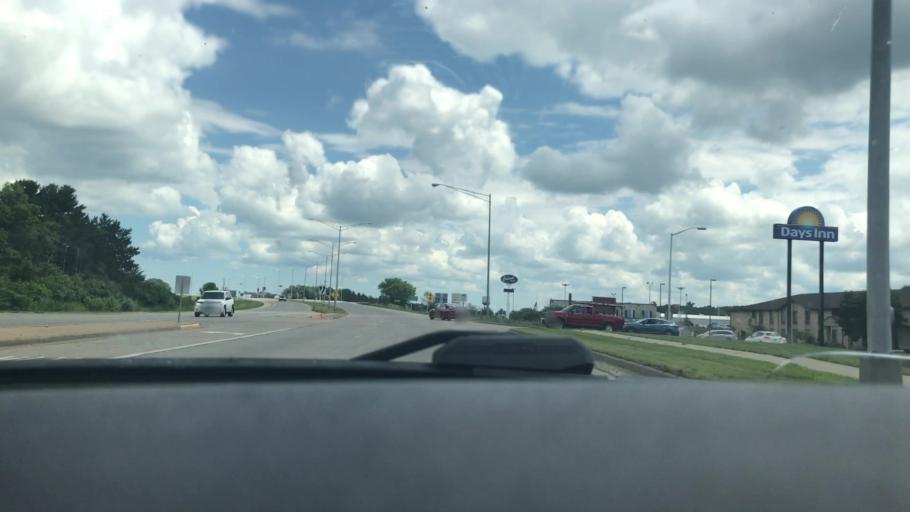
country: US
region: Wisconsin
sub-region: Jackson County
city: Black River Falls
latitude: 44.2944
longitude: -90.8291
